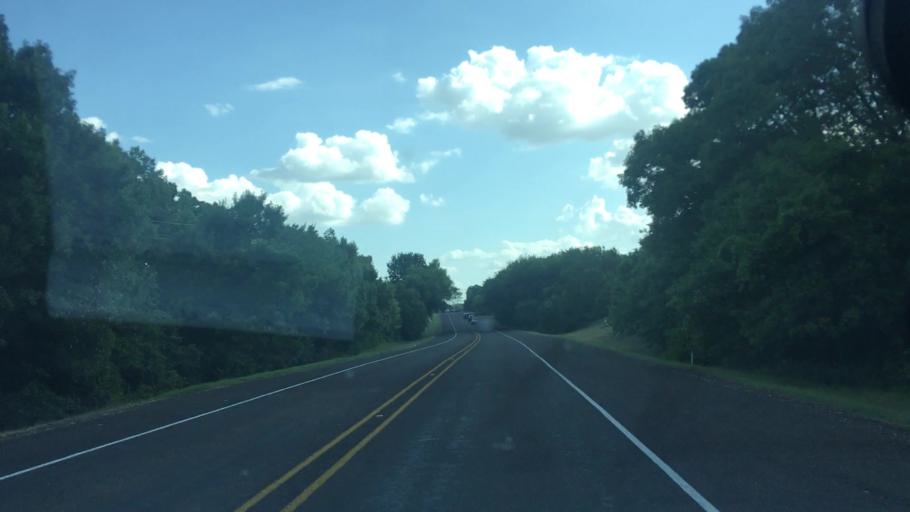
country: US
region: Texas
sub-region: Dallas County
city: Lancaster
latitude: 32.5748
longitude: -96.7589
